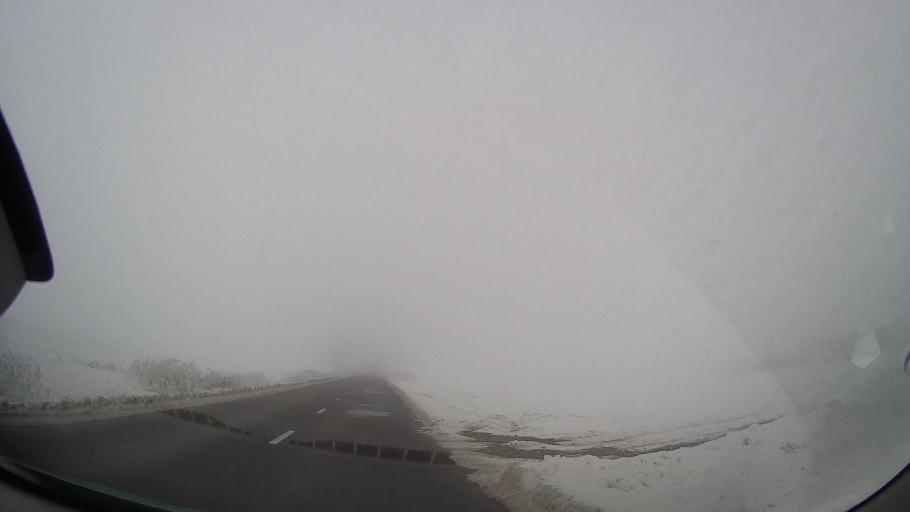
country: RO
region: Neamt
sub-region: Comuna Sabaoani
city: Sabaoani
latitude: 47.0382
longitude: 26.8531
